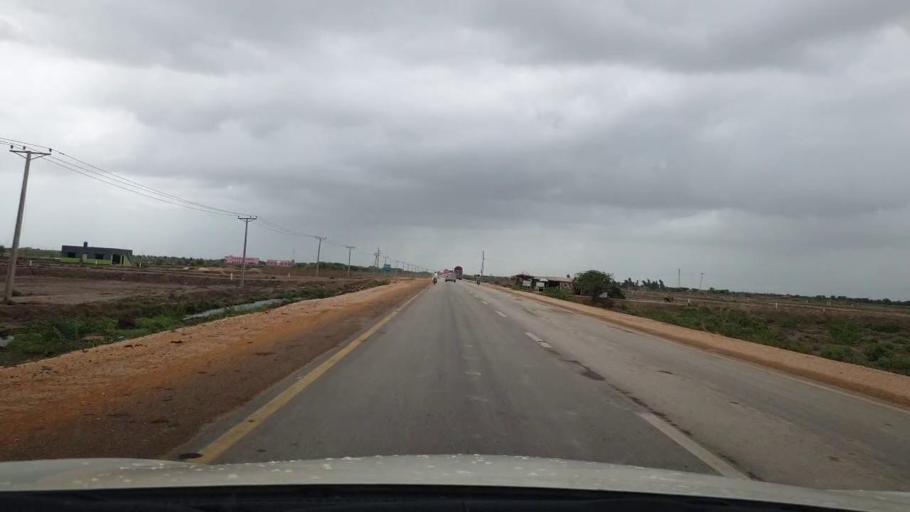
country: PK
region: Sindh
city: Badin
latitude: 24.6546
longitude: 68.7524
